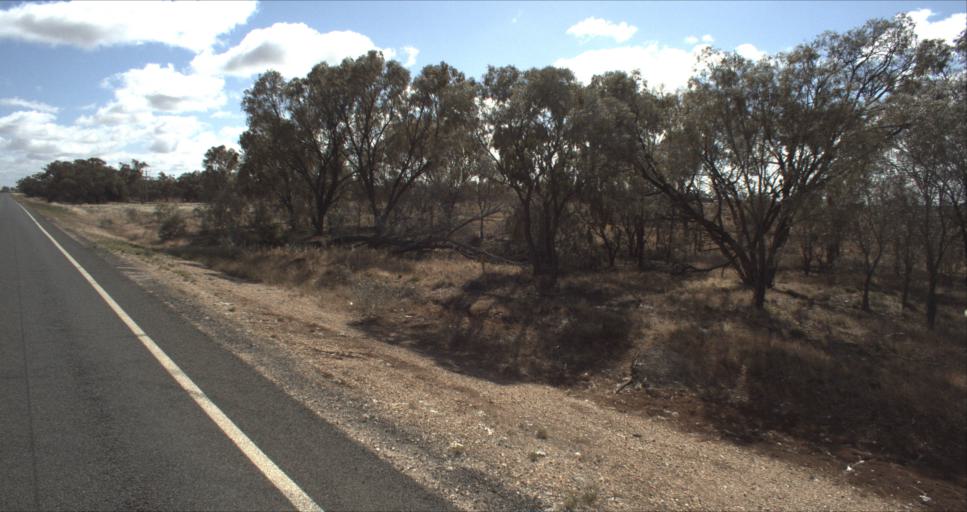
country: AU
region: New South Wales
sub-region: Murrumbidgee Shire
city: Darlington Point
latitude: -34.5271
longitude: 146.1746
